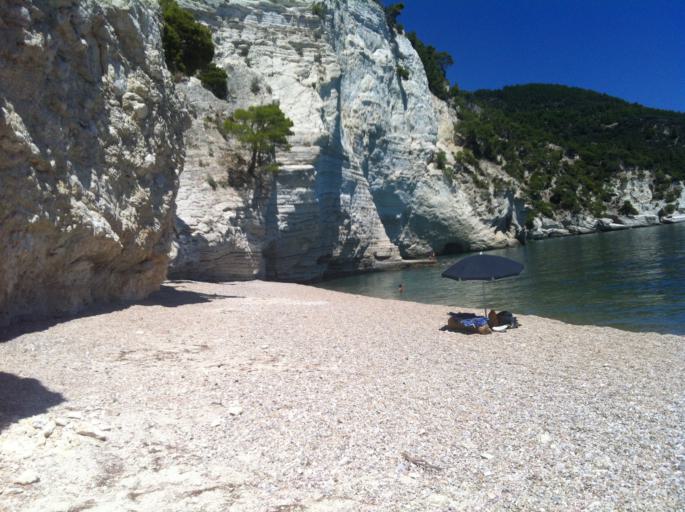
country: IT
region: Apulia
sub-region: Provincia di Foggia
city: Vieste
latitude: 41.7653
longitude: 16.1665
